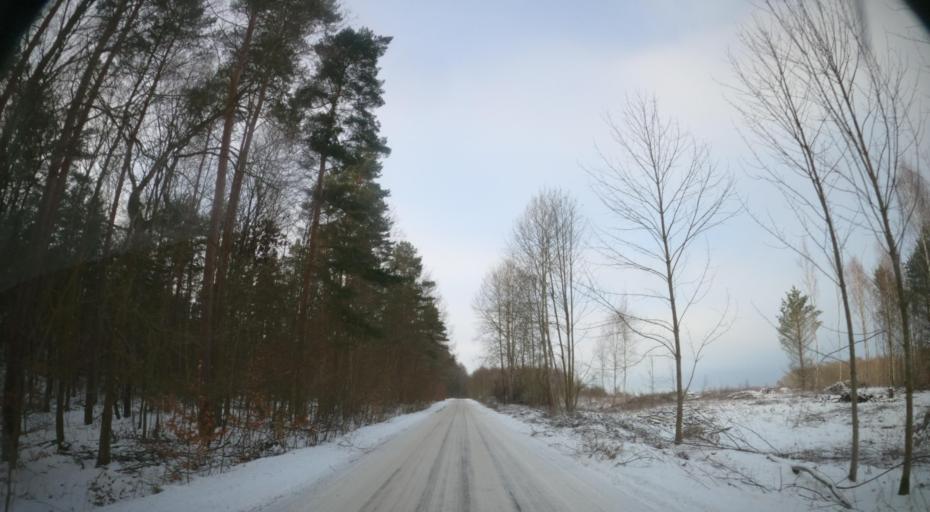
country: PL
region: West Pomeranian Voivodeship
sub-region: Powiat slawienski
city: Darlowo
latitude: 54.2855
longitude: 16.4437
